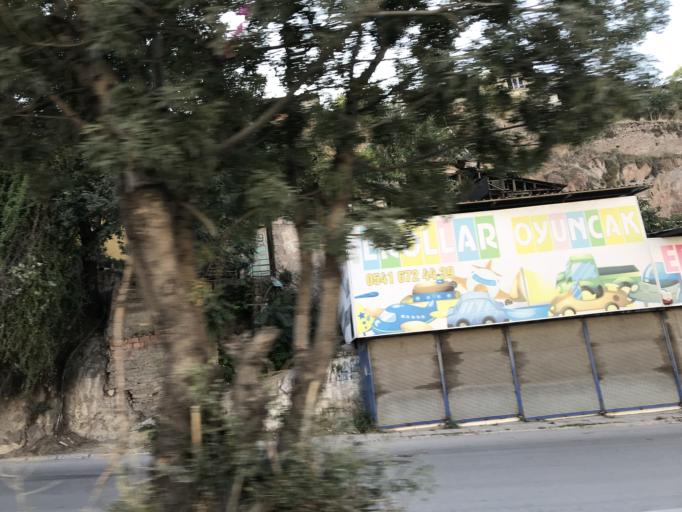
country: TR
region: Ankara
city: Cankaya
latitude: 39.9404
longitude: 32.8719
